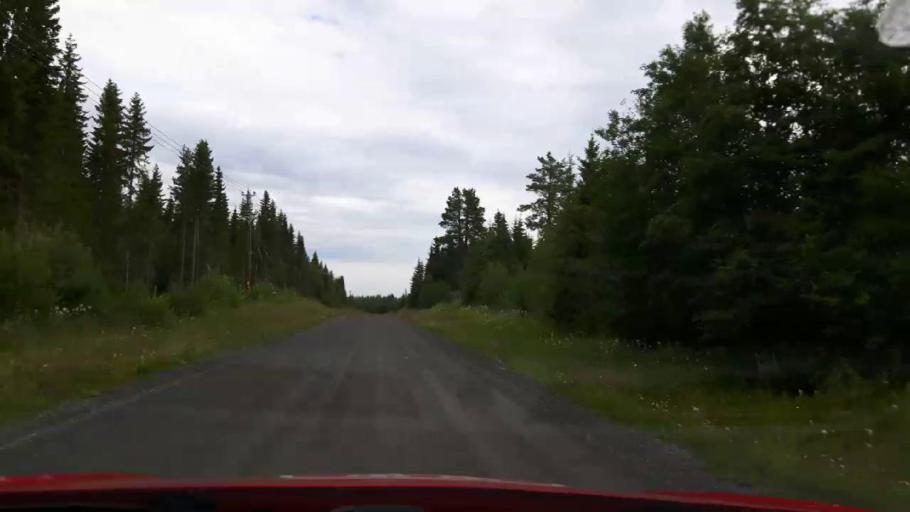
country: SE
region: Jaemtland
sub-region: Stroemsunds Kommun
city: Stroemsund
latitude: 63.4911
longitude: 15.3120
